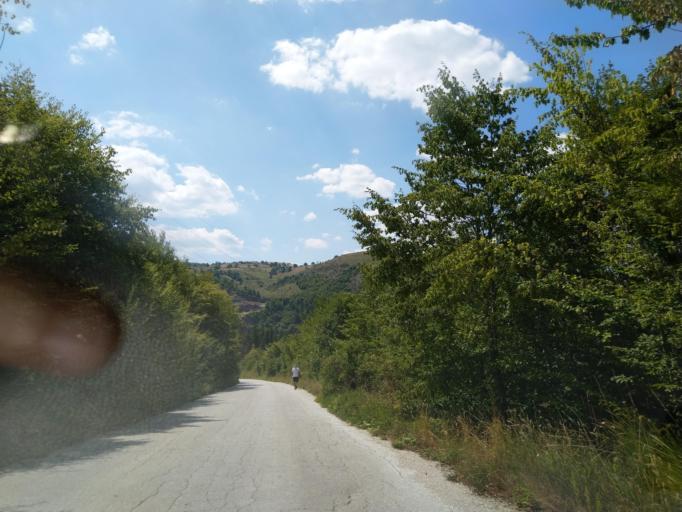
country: RS
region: Central Serbia
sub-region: Zlatiborski Okrug
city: Nova Varos
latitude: 43.4206
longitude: 19.9331
